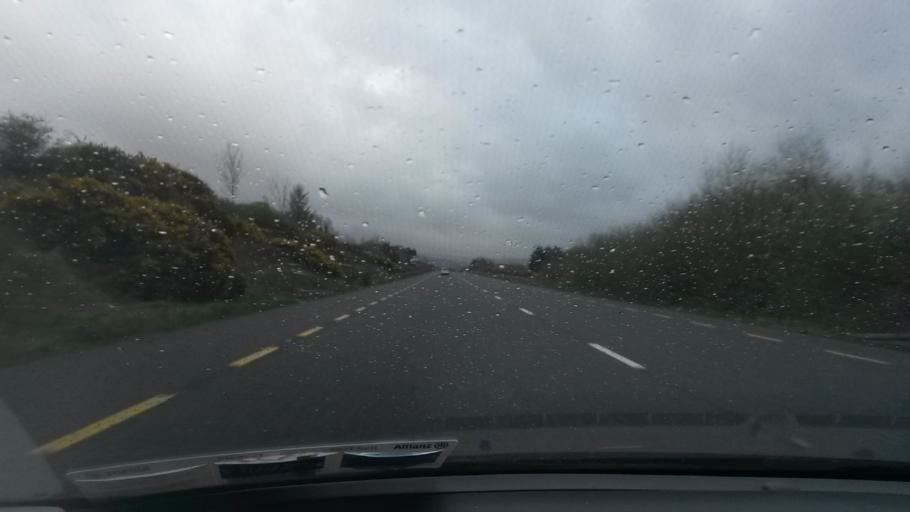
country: IE
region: Munster
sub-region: County Limerick
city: Abbeyfeale
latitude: 52.3261
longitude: -9.3592
